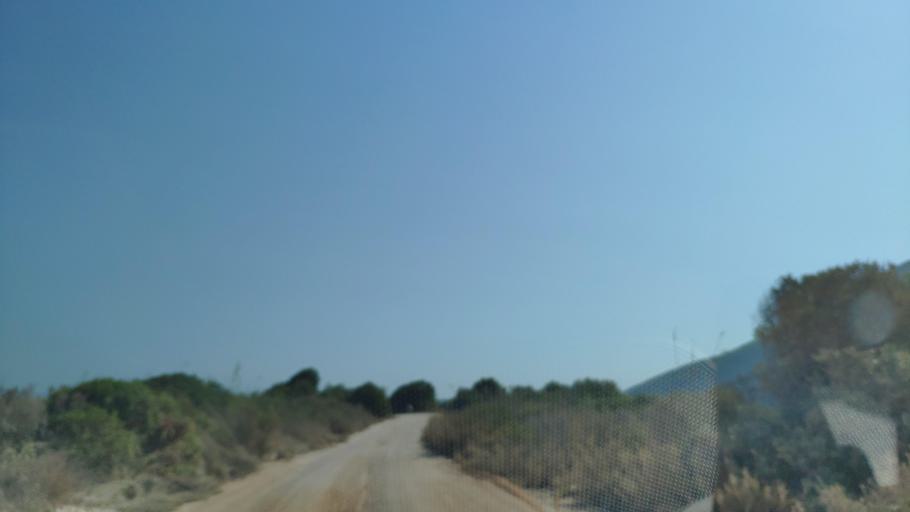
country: GR
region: Ionian Islands
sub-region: Lefkada
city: Lefkada
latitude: 38.8498
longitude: 20.7365
